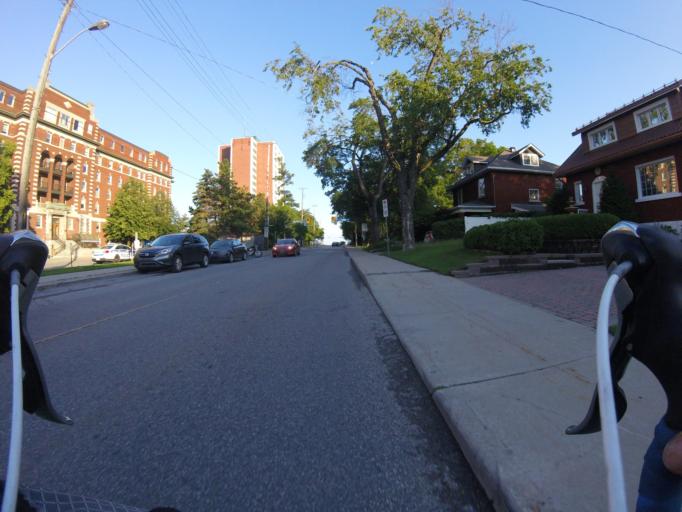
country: CA
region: Ontario
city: Ottawa
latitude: 45.3925
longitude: -75.7242
